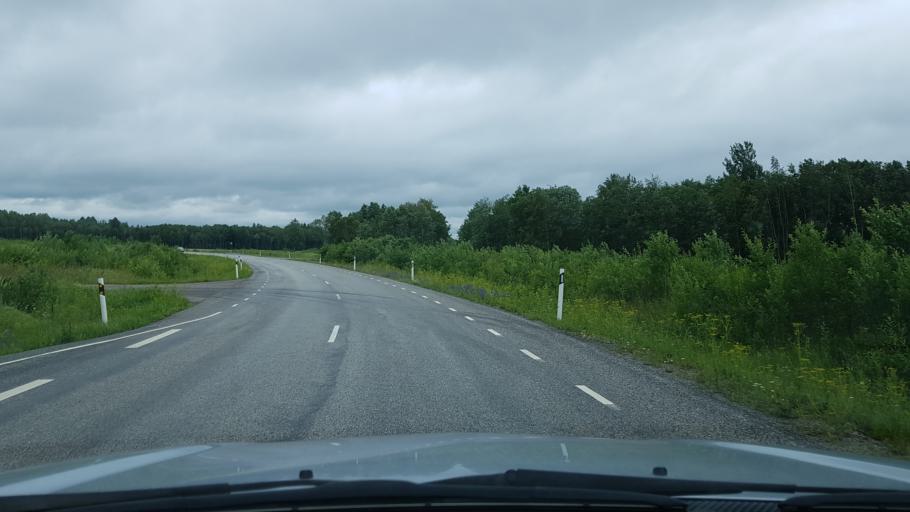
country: EE
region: Ida-Virumaa
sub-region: Narva-Joesuu linn
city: Narva-Joesuu
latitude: 59.3708
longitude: 27.9294
